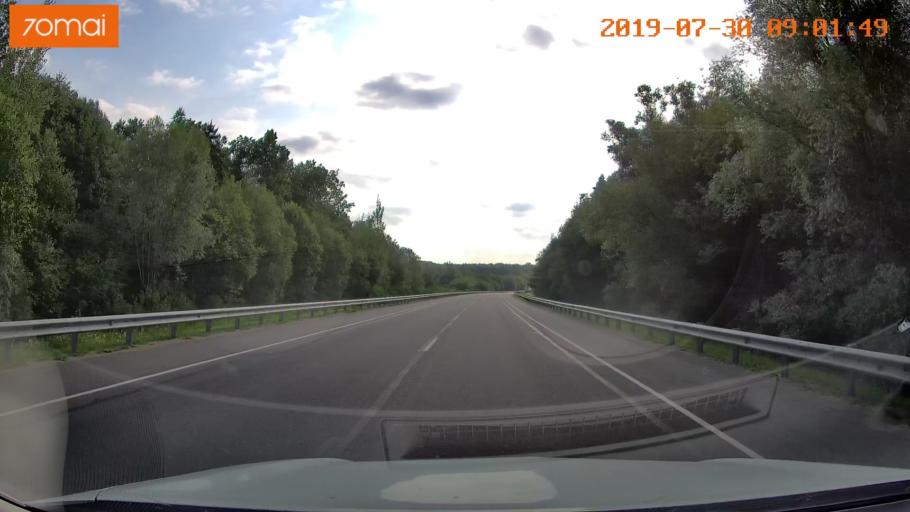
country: RU
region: Kaliningrad
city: Gusev
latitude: 54.6175
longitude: 22.2157
